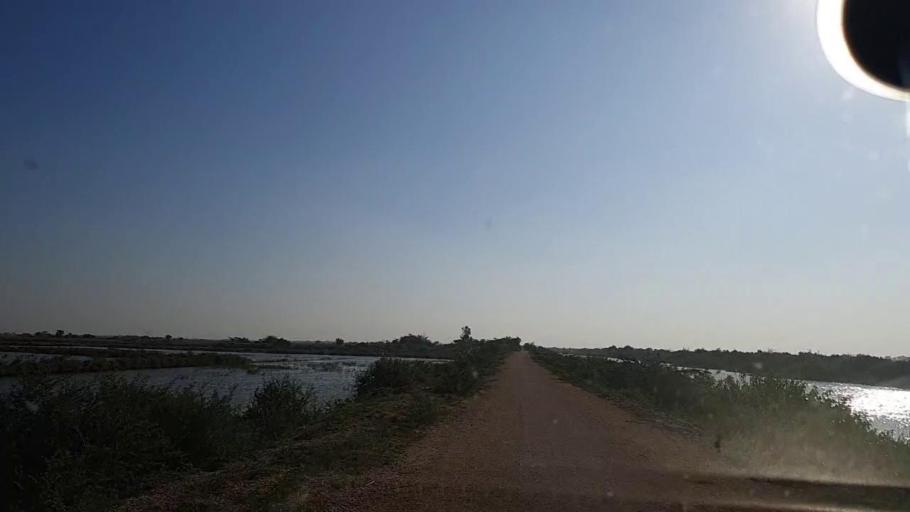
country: PK
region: Sindh
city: Chuhar Jamali
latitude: 24.5593
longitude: 68.0388
